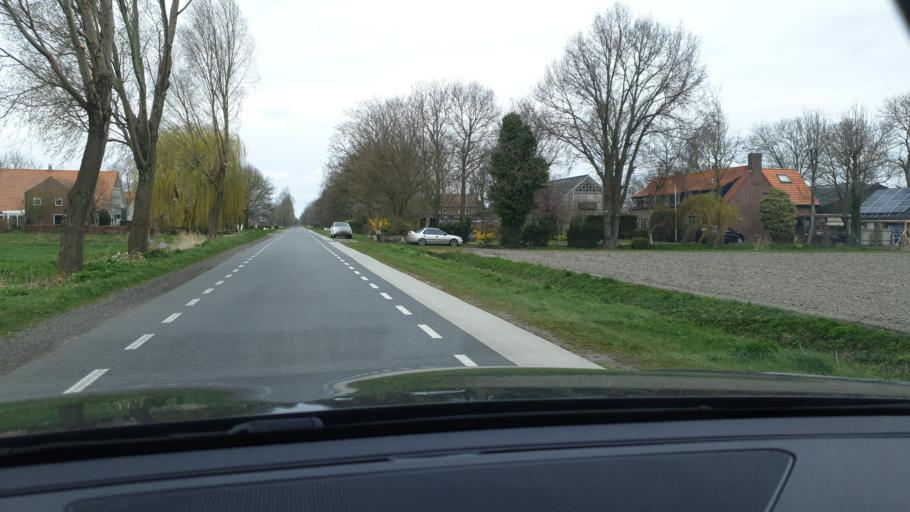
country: NL
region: Friesland
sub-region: Gemeente Lemsterland
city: Lemmer
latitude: 52.7721
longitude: 5.6463
